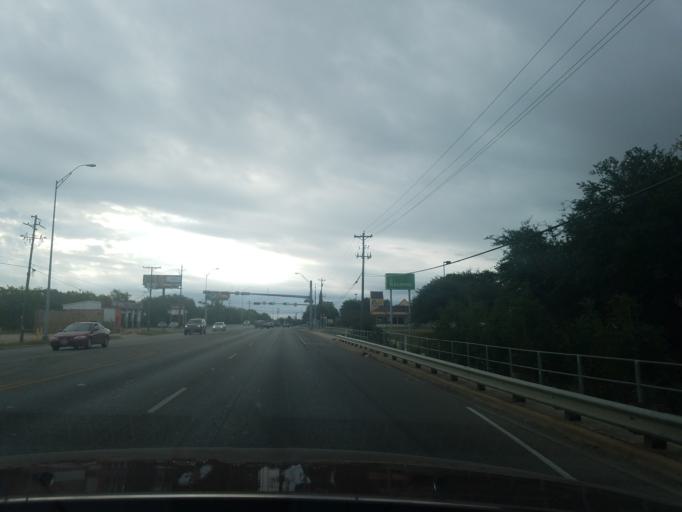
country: US
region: Texas
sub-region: Williamson County
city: Cedar Park
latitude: 30.5145
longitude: -97.8259
